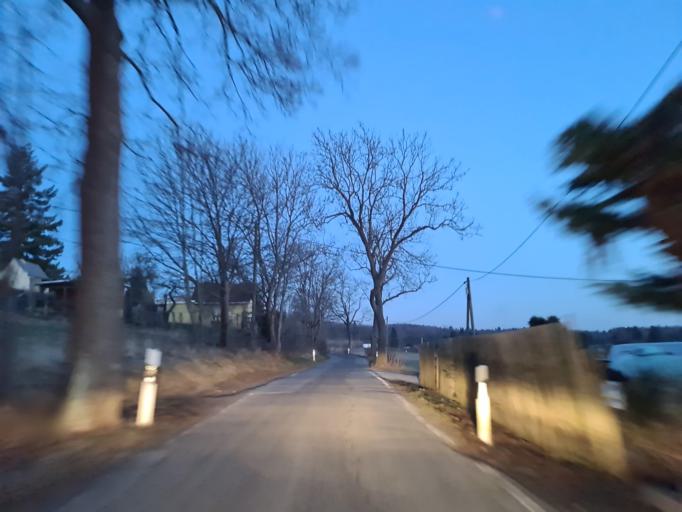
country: DE
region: Saxony
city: Syrau
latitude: 50.5197
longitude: 12.1016
